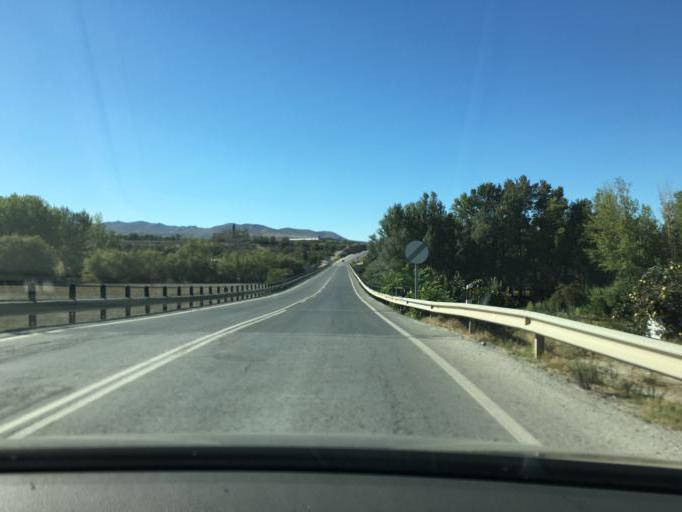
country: ES
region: Andalusia
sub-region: Provincia de Granada
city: Caniles
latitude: 37.4461
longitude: -2.7253
